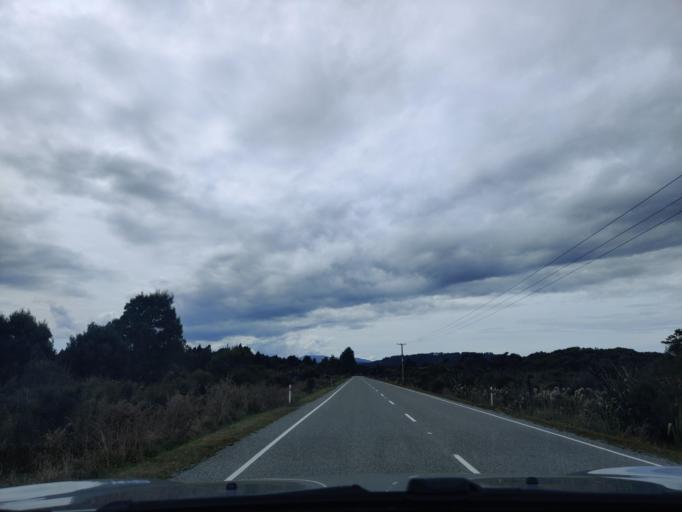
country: NZ
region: West Coast
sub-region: Grey District
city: Greymouth
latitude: -42.5779
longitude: 171.1394
